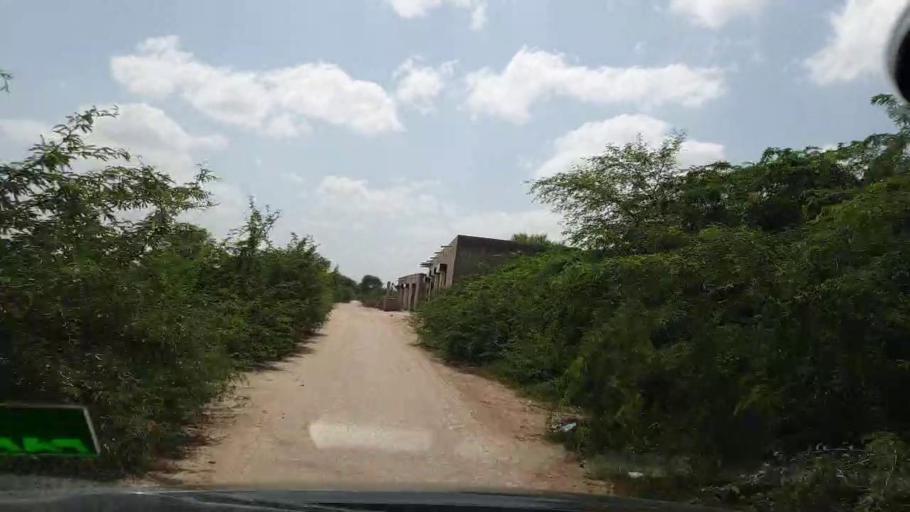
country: PK
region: Sindh
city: Kadhan
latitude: 24.5638
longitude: 69.2110
